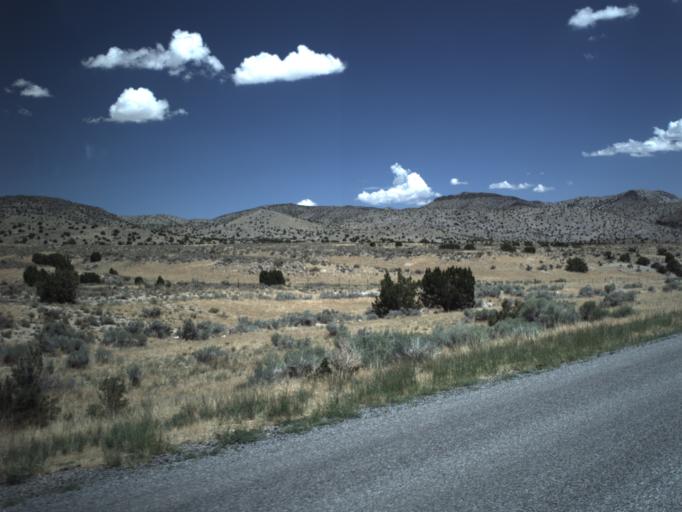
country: US
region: Utah
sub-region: Beaver County
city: Milford
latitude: 39.0761
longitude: -113.6295
